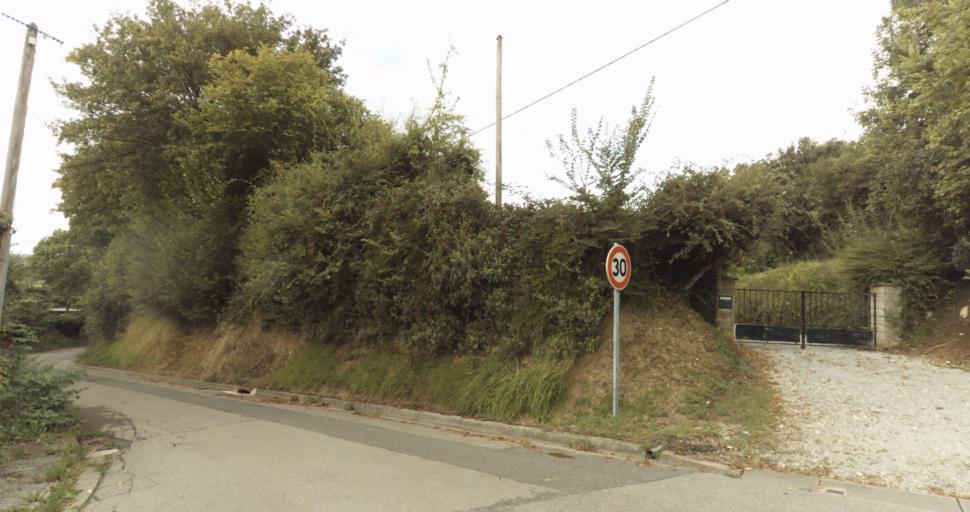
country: FR
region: Lower Normandy
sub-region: Departement de l'Orne
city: Gace
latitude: 48.7962
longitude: 0.3053
